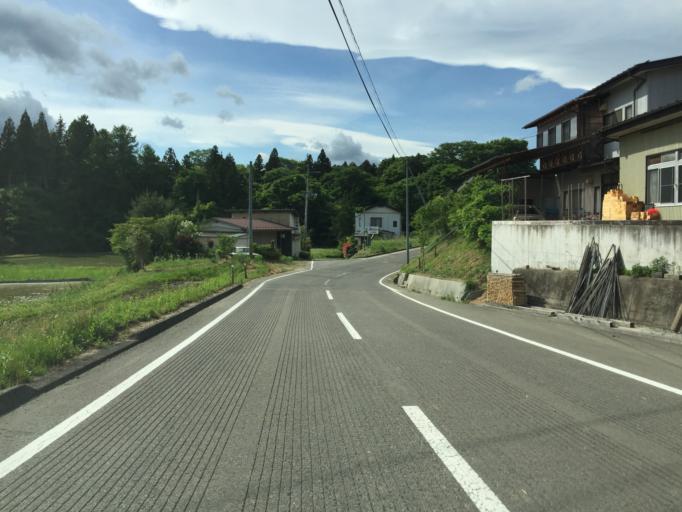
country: JP
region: Fukushima
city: Nihommatsu
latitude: 37.5946
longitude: 140.5176
